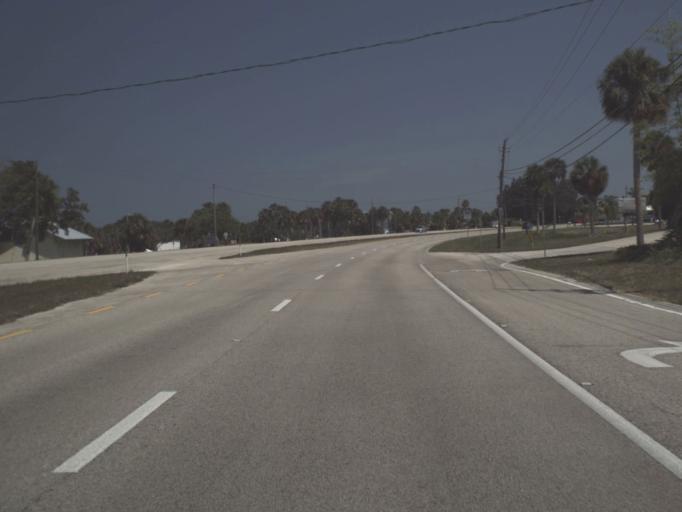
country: US
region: Florida
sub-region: Brevard County
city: Micco
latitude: 27.9227
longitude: -80.5220
